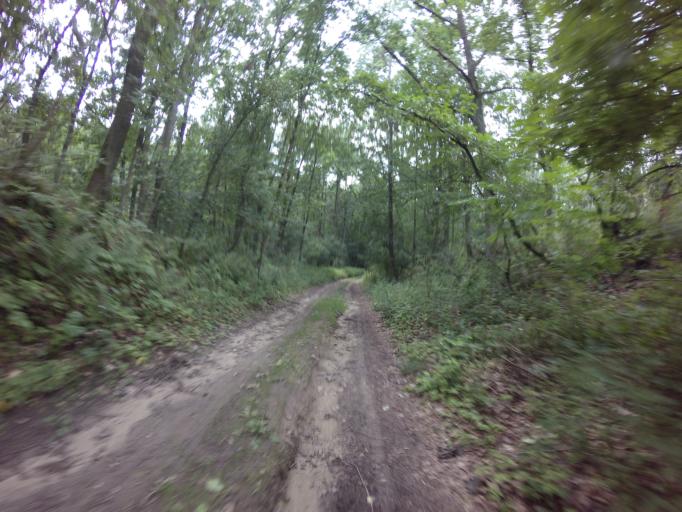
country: PL
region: Kujawsko-Pomorskie
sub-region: Powiat bydgoski
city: Koronowo
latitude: 53.3766
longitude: 17.9969
